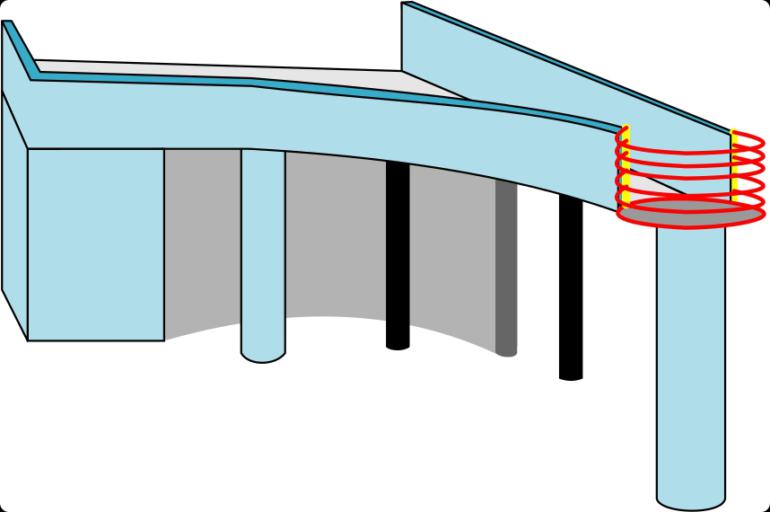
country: HU
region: Baranya
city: Pecs
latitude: 46.1028
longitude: 18.2079
